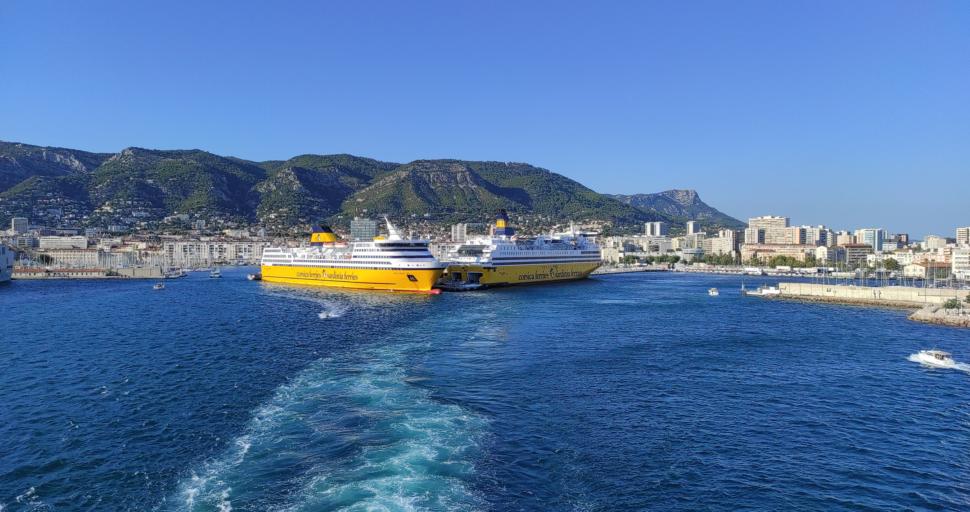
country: FR
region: Provence-Alpes-Cote d'Azur
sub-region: Departement du Var
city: Toulon
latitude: 43.1133
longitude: 5.9268
